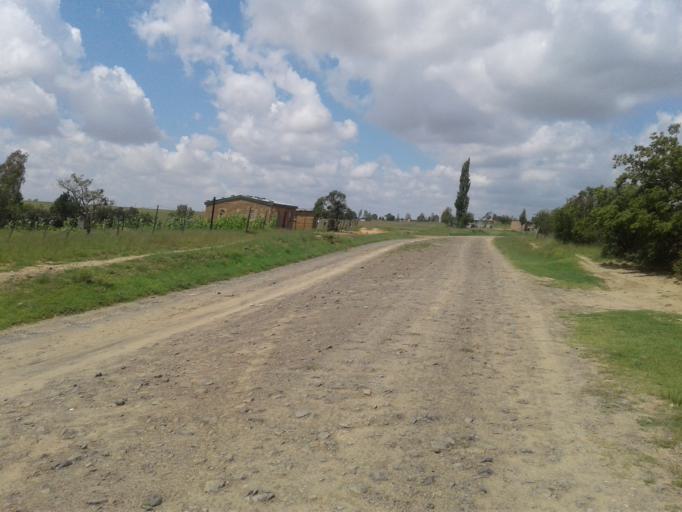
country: LS
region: Mafeteng
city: Mafeteng
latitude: -29.7485
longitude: 27.1137
